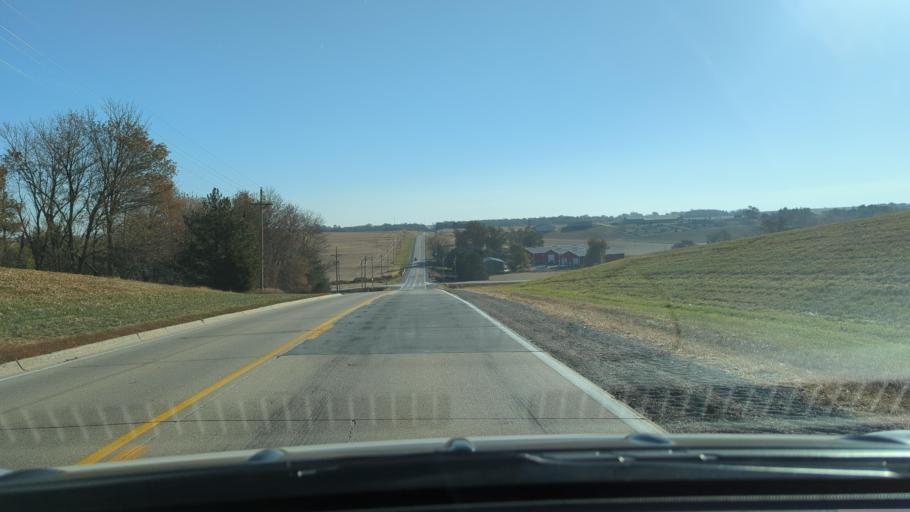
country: US
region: Nebraska
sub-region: Sarpy County
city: Papillion
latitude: 41.0927
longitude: -96.0123
